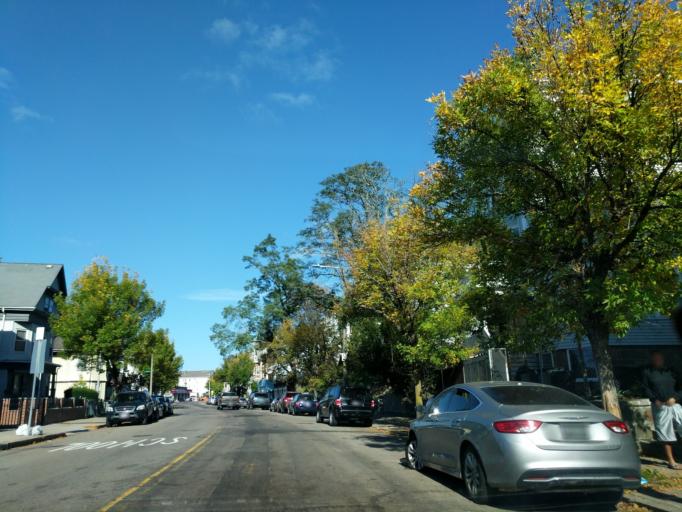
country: US
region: Massachusetts
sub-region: Suffolk County
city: South Boston
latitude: 42.3116
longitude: -71.0631
